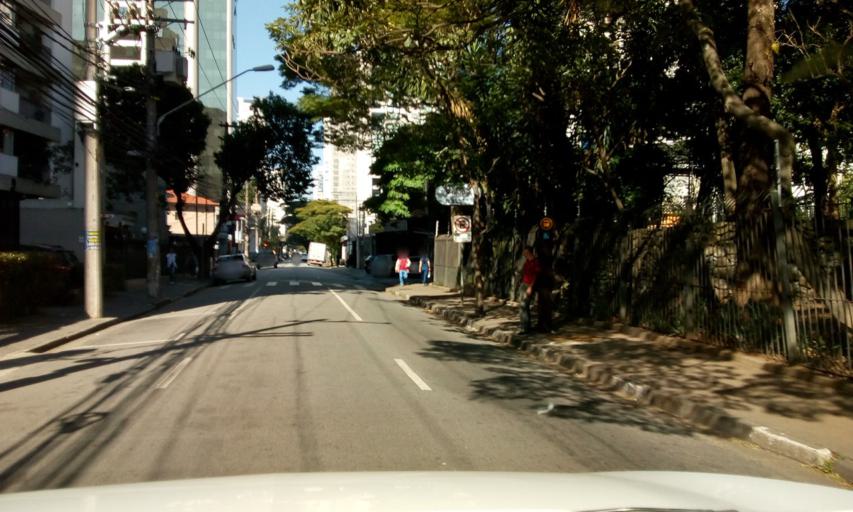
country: BR
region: Sao Paulo
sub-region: Sao Paulo
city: Sao Paulo
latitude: -23.5989
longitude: -46.6839
